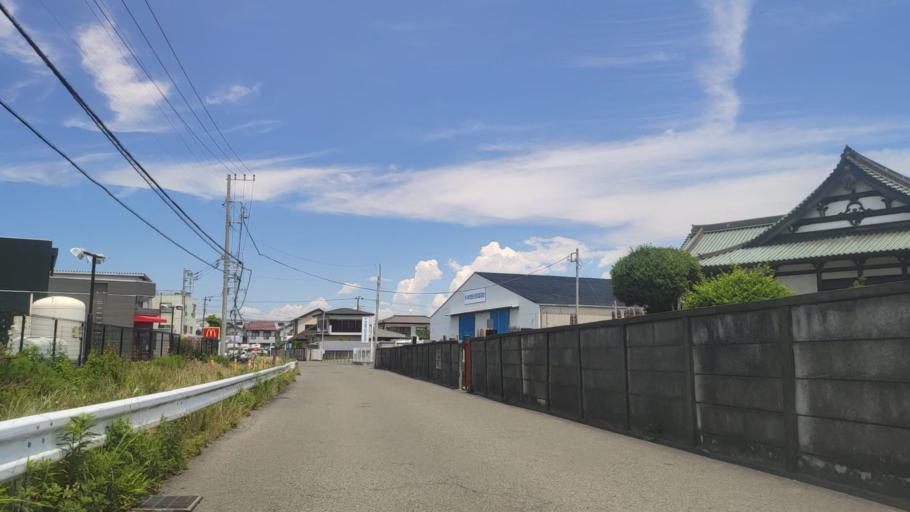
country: JP
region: Kanagawa
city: Chigasaki
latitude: 35.3332
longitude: 139.3776
